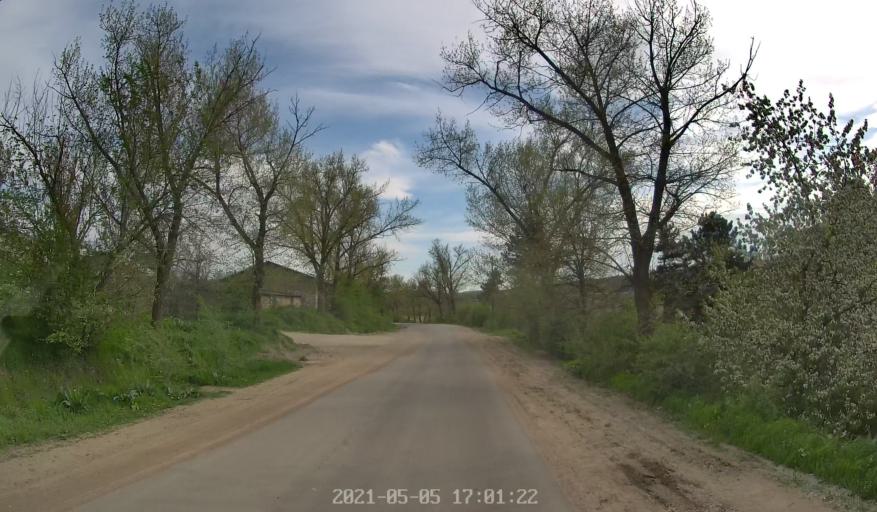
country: MD
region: Chisinau
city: Vadul lui Voda
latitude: 47.0588
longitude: 29.1324
